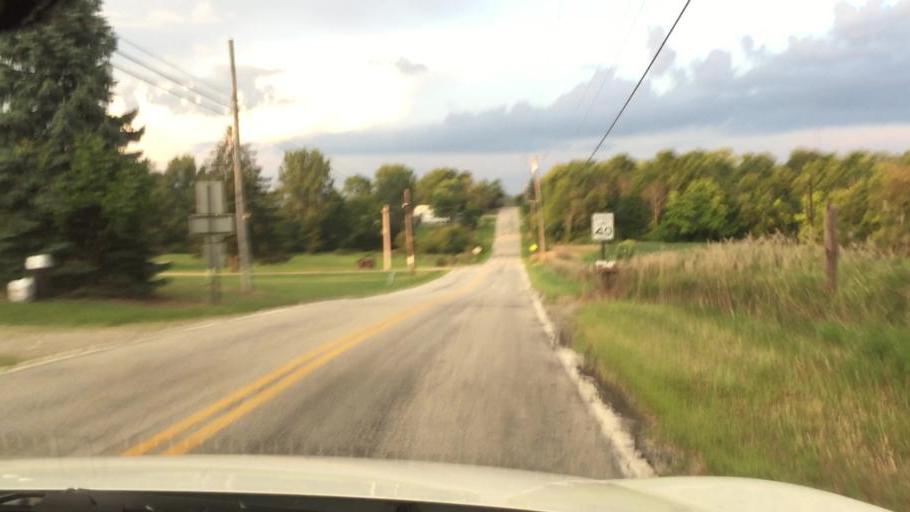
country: US
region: Ohio
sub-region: Champaign County
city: Mechanicsburg
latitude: 40.0031
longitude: -83.6167
